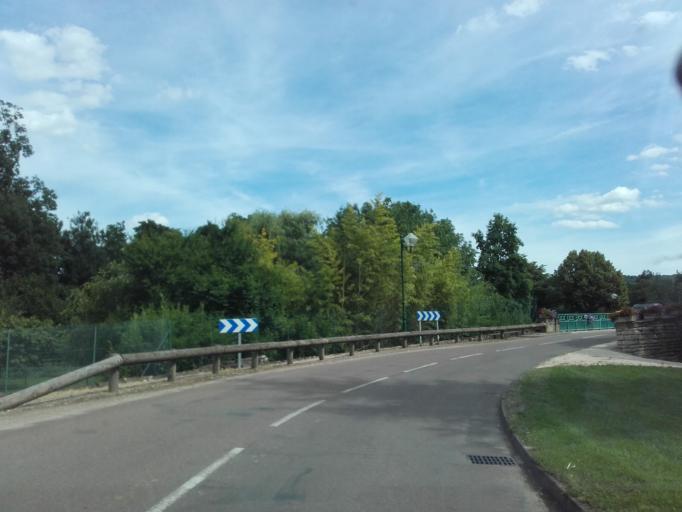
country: FR
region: Bourgogne
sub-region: Departement de Saone-et-Loire
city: Chagny
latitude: 46.9087
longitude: 4.7063
